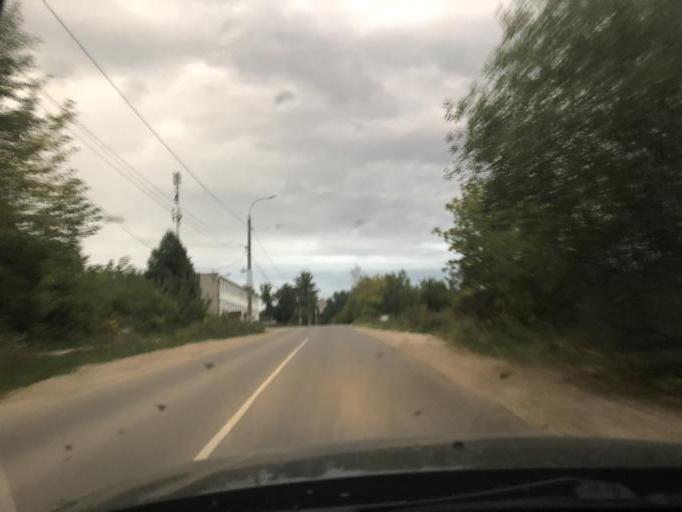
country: RU
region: Tula
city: Gorelki
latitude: 54.2259
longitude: 37.6020
